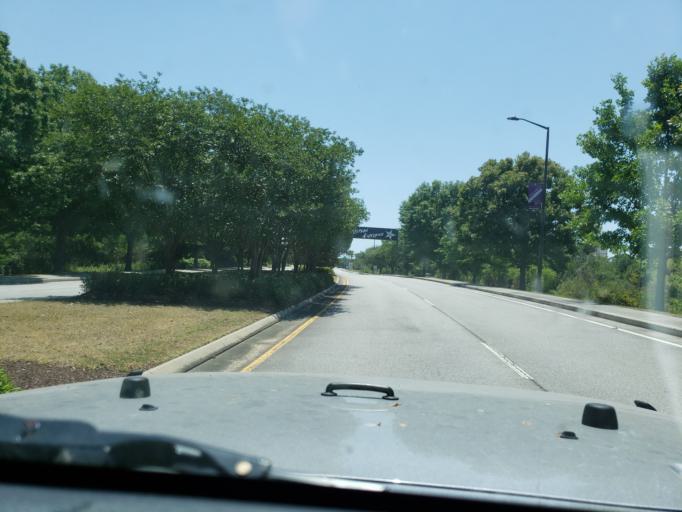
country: US
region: Georgia
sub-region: Chatham County
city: Savannah
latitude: 32.0903
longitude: -81.0890
